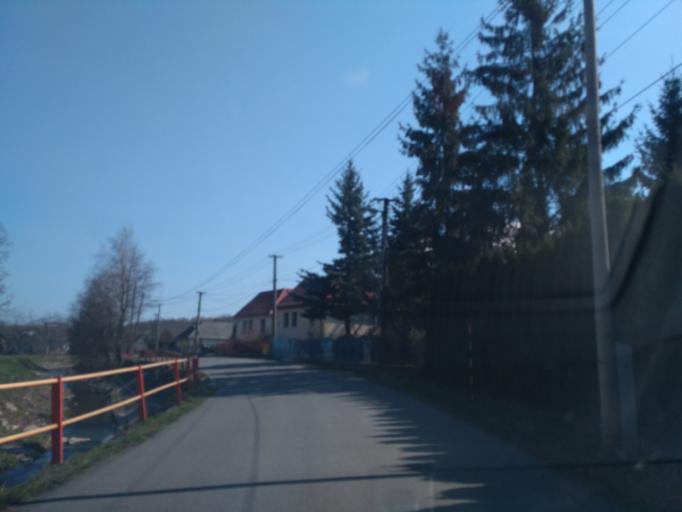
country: SK
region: Presovsky
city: Vranov nad Topl'ou
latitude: 48.8251
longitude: 21.6335
